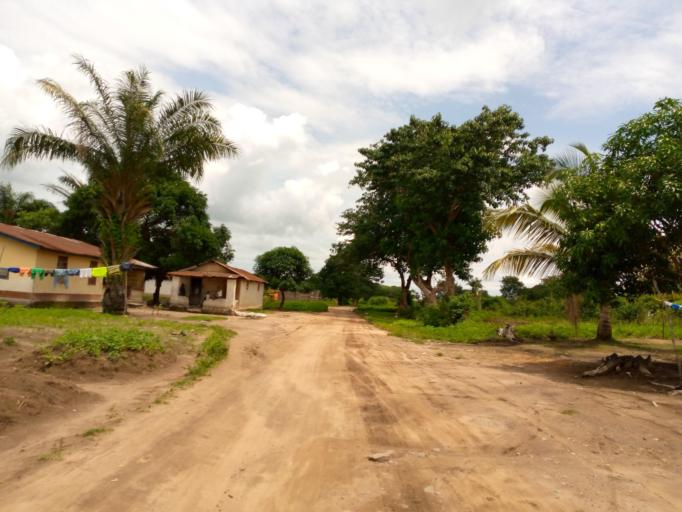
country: SL
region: Northern Province
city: Magburaka
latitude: 8.7121
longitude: -11.9618
